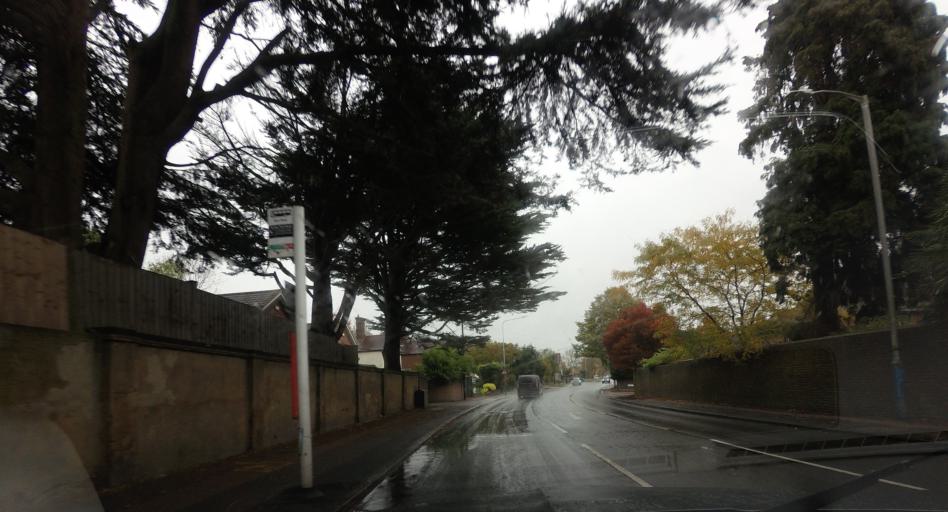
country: GB
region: England
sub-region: Kent
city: Tonbridge
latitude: 51.2030
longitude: 0.2866
